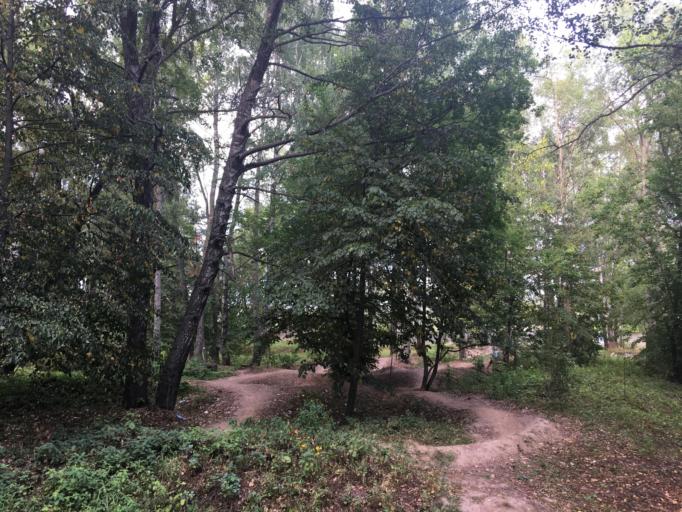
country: RU
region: Nizjnij Novgorod
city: Lyskovo
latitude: 56.0271
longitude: 45.0535
